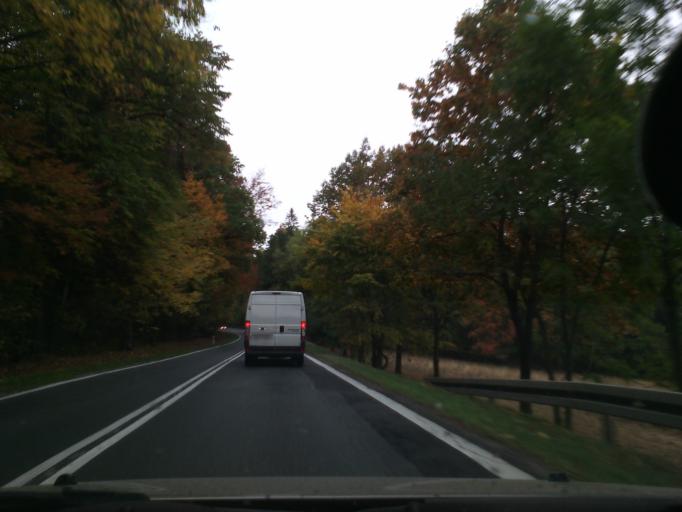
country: PL
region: Lower Silesian Voivodeship
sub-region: Powiat jaworski
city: Bolkow
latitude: 50.9409
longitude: 16.0341
